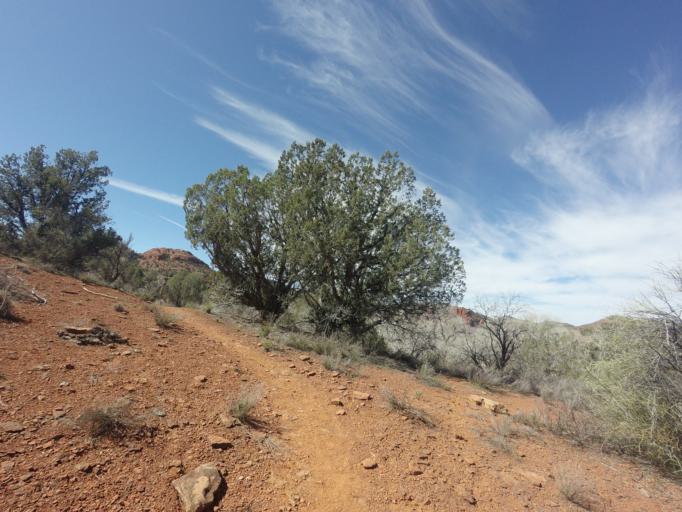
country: US
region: Arizona
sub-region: Yavapai County
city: West Sedona
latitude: 34.8102
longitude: -111.8233
